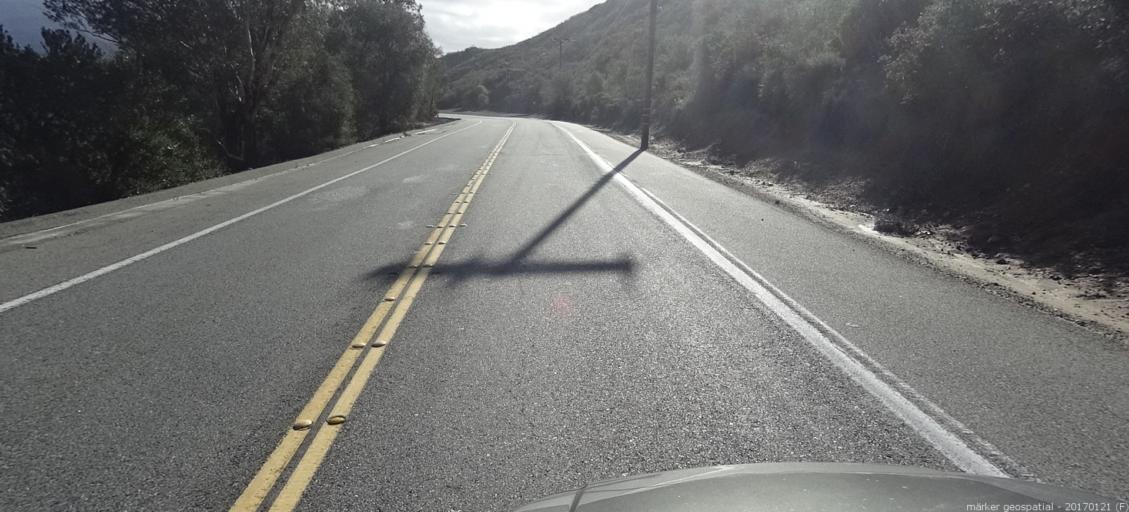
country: US
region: California
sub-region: Orange County
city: Foothill Ranch
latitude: 33.7489
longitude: -117.6793
